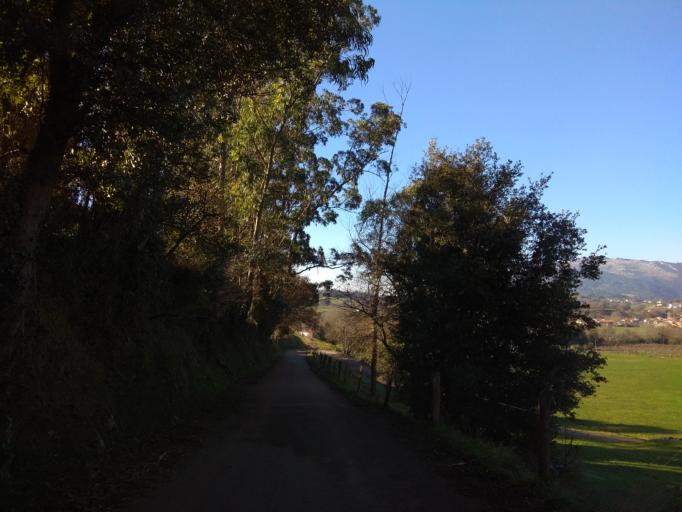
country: ES
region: Cantabria
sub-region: Provincia de Cantabria
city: Entrambasaguas
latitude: 43.3721
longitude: -3.7061
